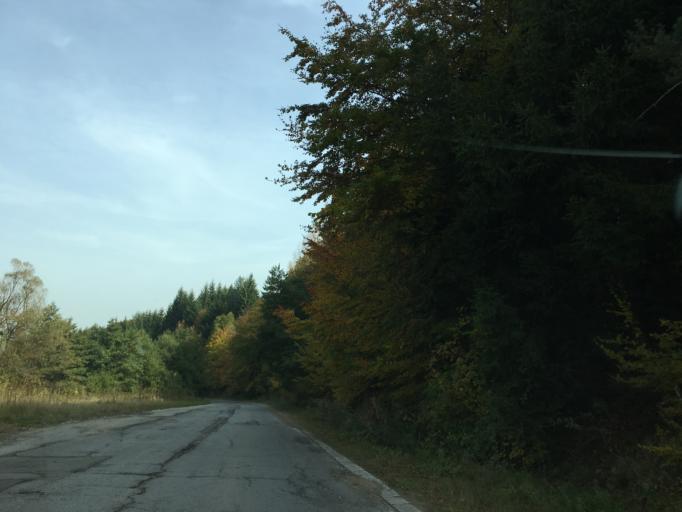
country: BG
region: Sofiya
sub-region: Obshtina Dolna Banya
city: Dolna Banya
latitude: 42.2788
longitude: 23.6655
